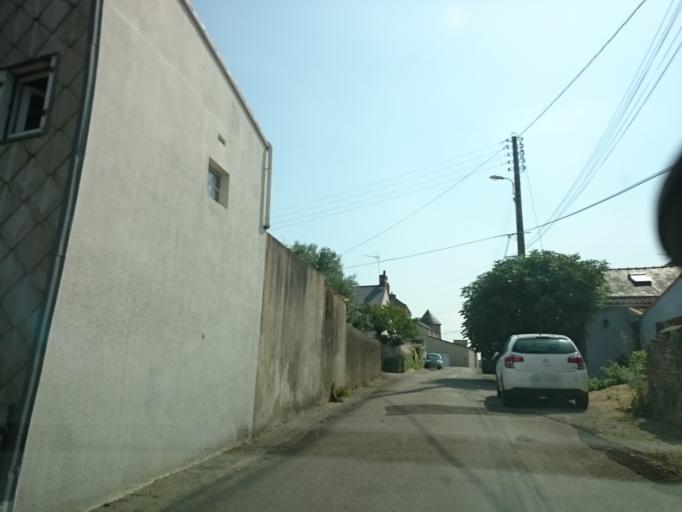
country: FR
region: Pays de la Loire
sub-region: Departement de la Loire-Atlantique
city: La Montagne
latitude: 47.1933
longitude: -1.6902
